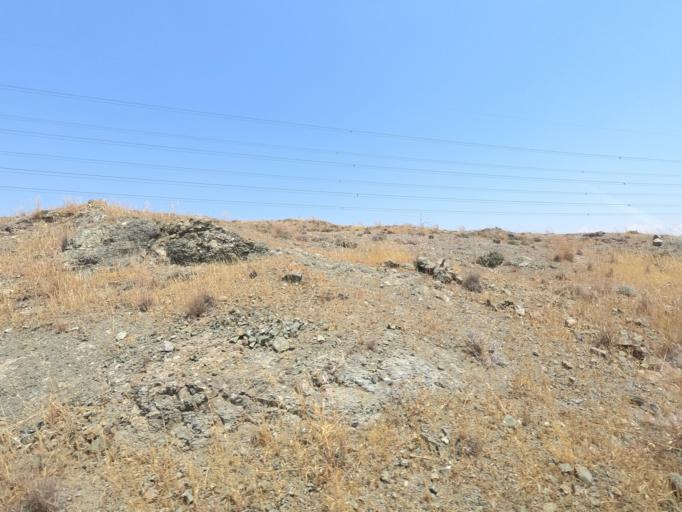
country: CY
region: Larnaka
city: Voroklini
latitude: 35.0008
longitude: 33.6249
